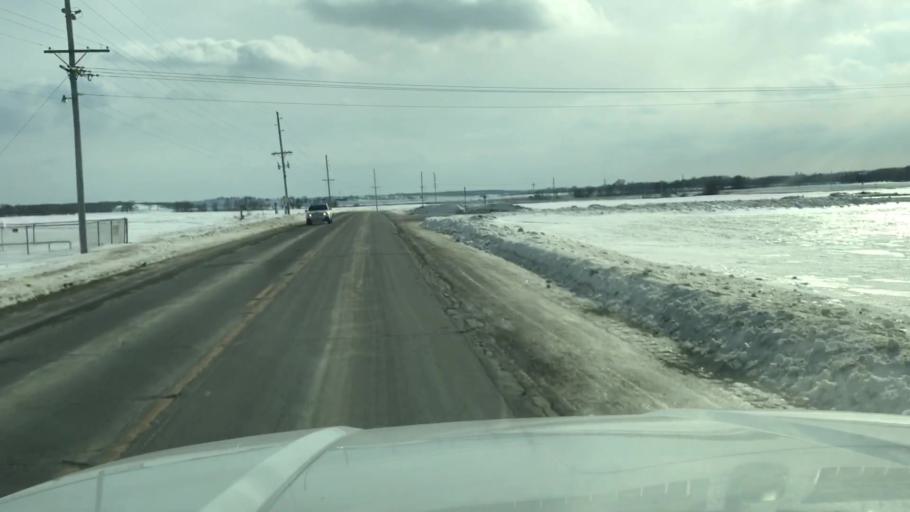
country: US
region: Missouri
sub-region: Gentry County
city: Stanberry
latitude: 40.3472
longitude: -94.6734
